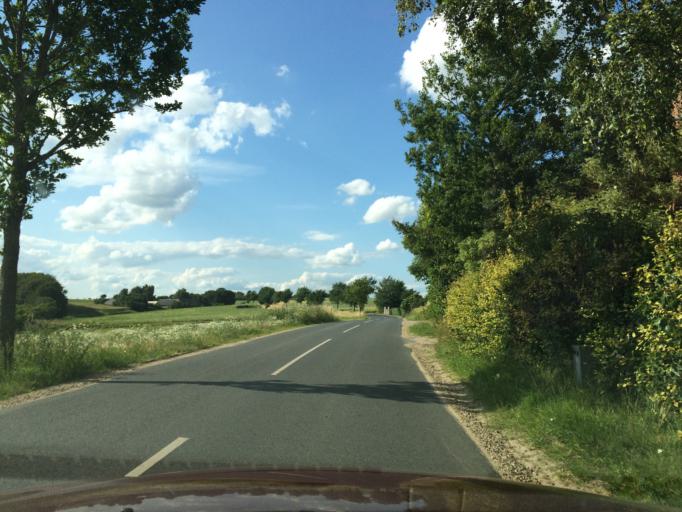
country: DK
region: Central Jutland
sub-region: Favrskov Kommune
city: Hammel
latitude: 56.2372
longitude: 9.7395
